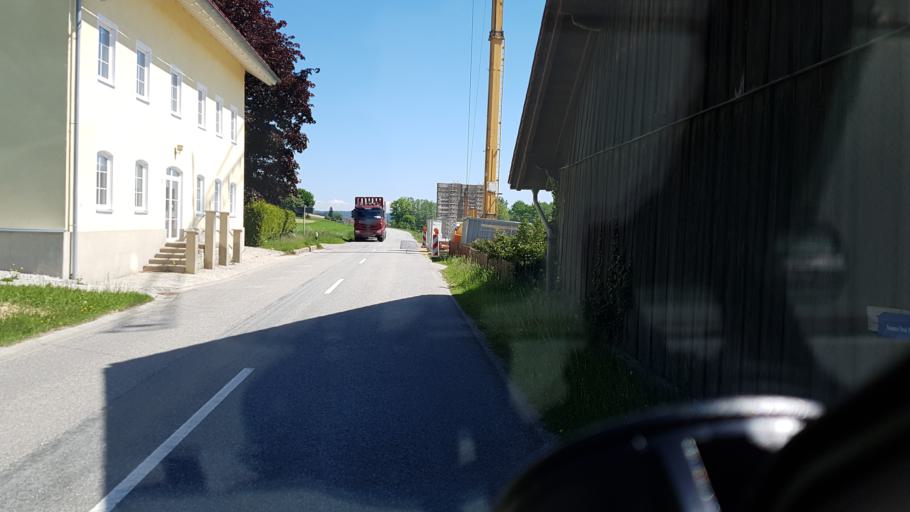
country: DE
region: Bavaria
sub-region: Lower Bavaria
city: Pfarrkirchen
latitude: 48.4001
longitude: 12.9304
